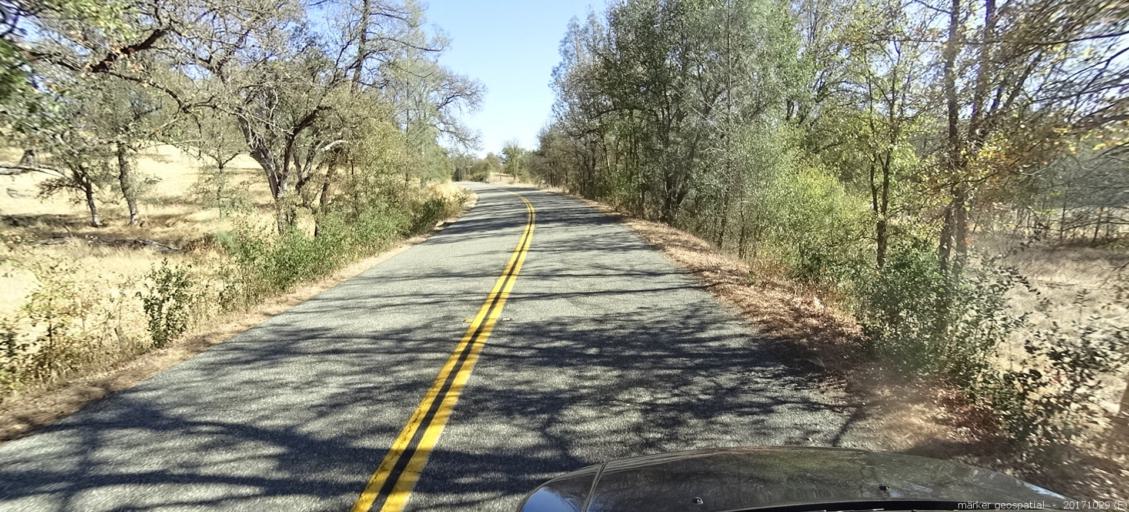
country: US
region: California
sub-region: Shasta County
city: Shasta
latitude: 40.4812
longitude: -122.5823
